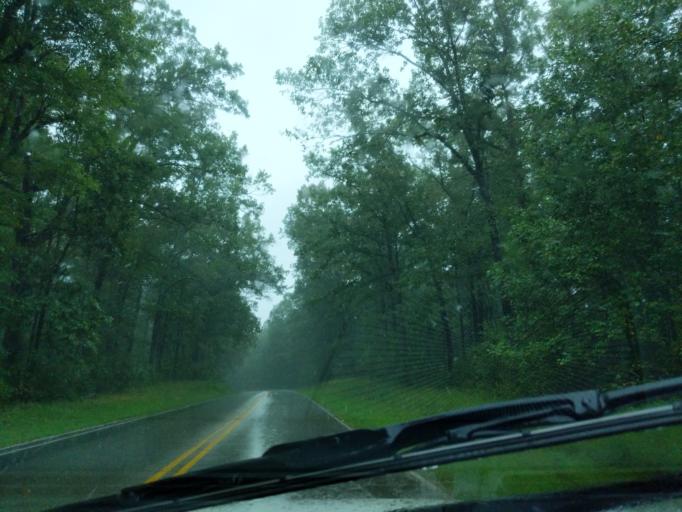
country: US
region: Kentucky
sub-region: Barren County
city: Cave City
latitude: 37.1777
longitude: -86.0894
